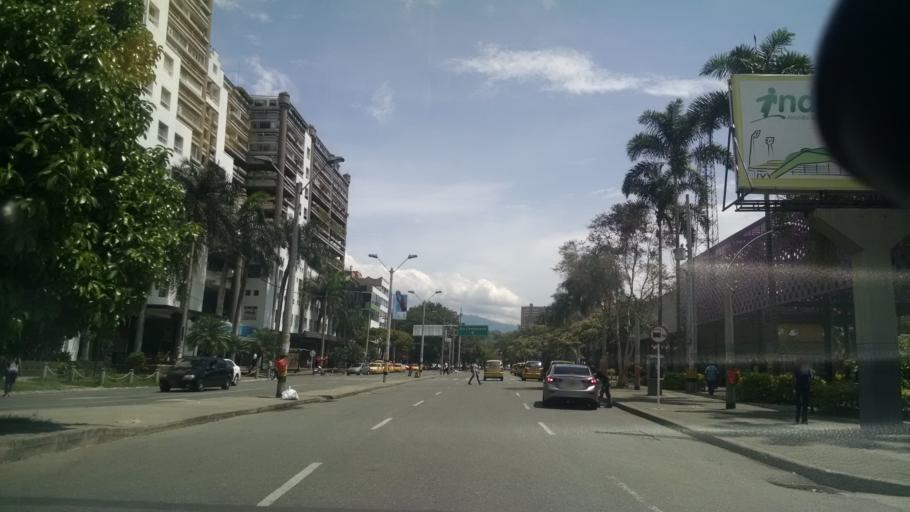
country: CO
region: Antioquia
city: Medellin
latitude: 6.2564
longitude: -75.5921
